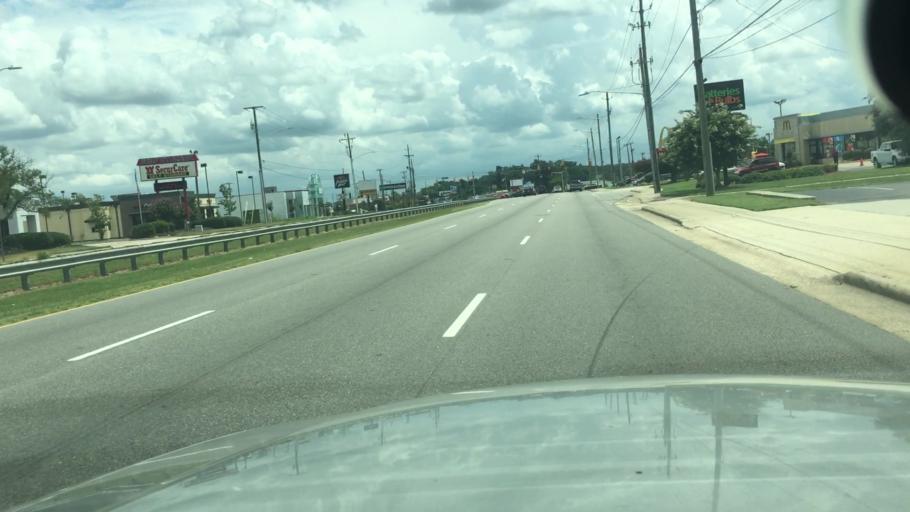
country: US
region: North Carolina
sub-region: Cumberland County
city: Fayetteville
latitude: 35.0794
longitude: -78.9413
